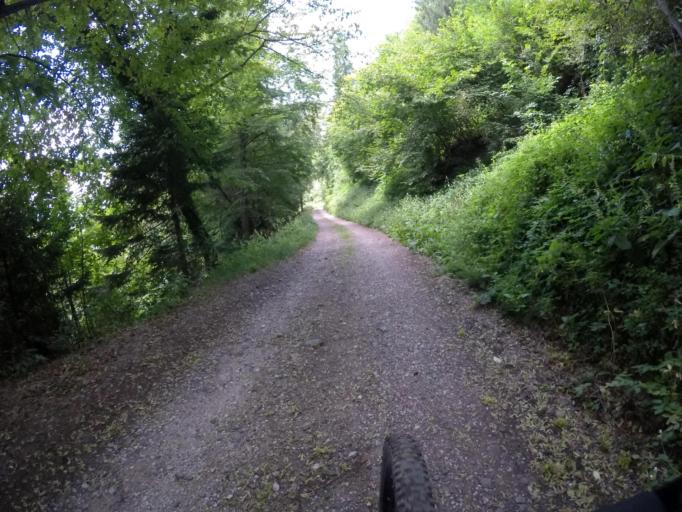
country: IT
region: Friuli Venezia Giulia
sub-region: Provincia di Udine
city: Zuglio
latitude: 46.4747
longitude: 13.0547
